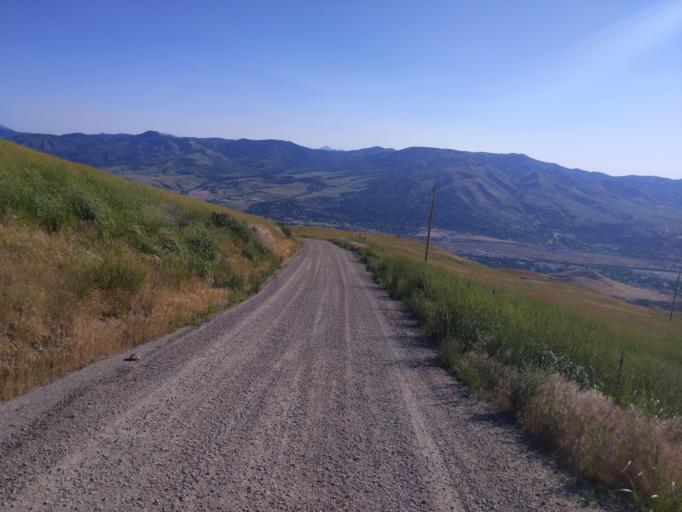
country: US
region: Idaho
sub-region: Bannock County
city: Pocatello
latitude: 42.8497
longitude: -112.3661
